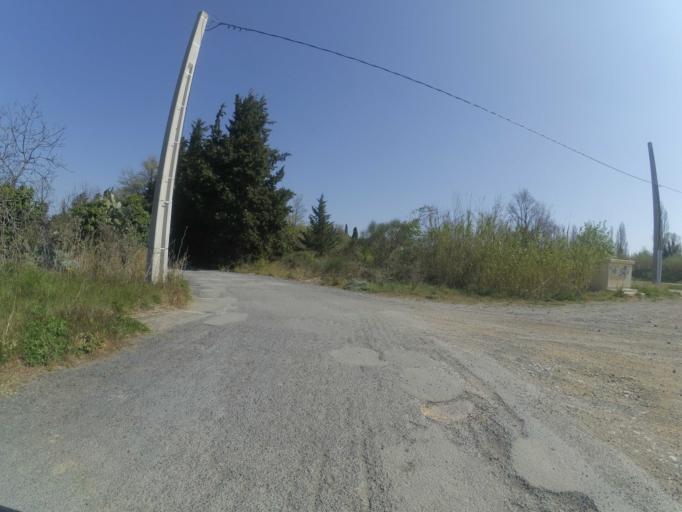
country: FR
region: Languedoc-Roussillon
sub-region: Departement des Pyrenees-Orientales
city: Pezilla-la-Riviere
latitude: 42.6680
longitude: 2.7602
